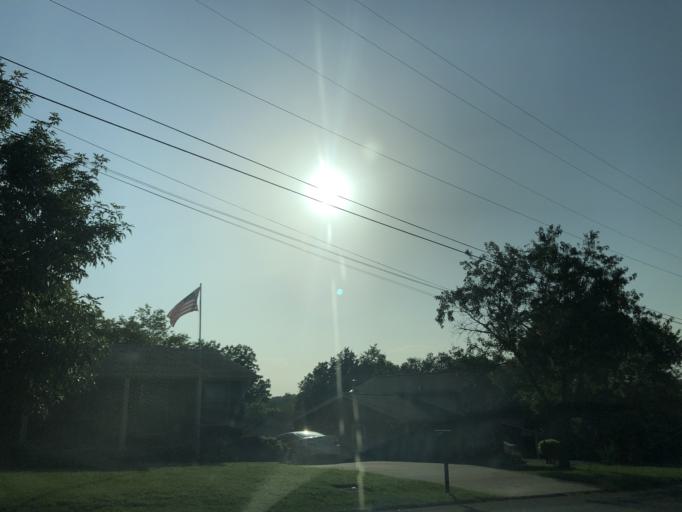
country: US
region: Tennessee
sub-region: Davidson County
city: Lakewood
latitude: 36.1502
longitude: -86.6490
